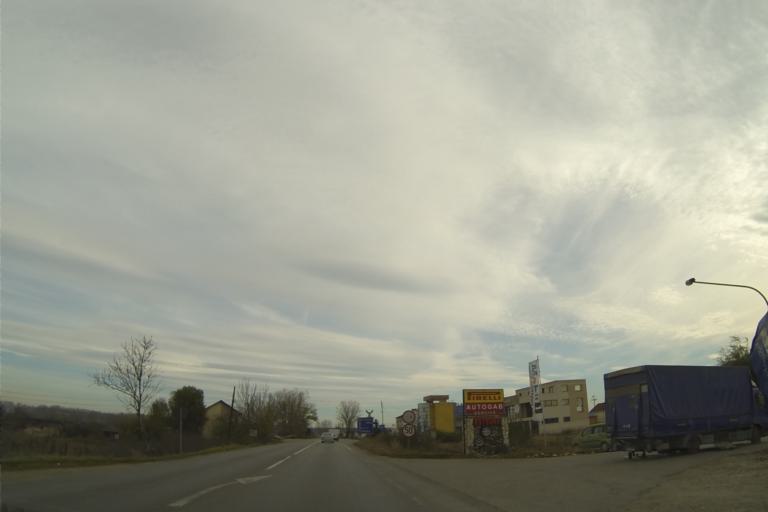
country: RO
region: Olt
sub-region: Comuna Slatioara
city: Slatioara
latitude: 44.4185
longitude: 24.3251
